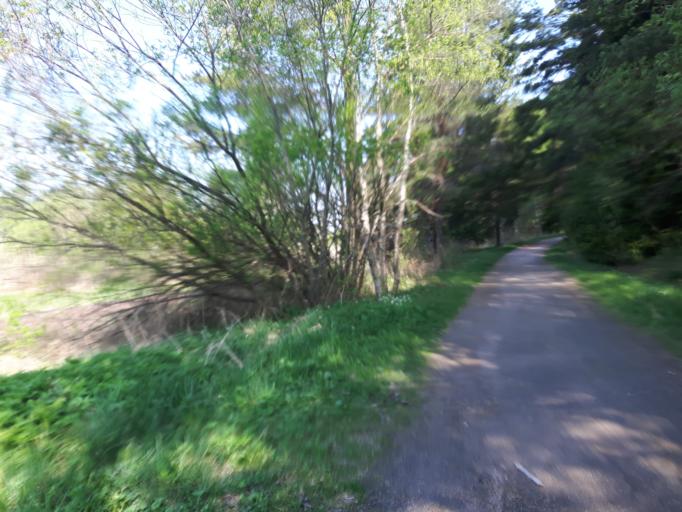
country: FI
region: Uusimaa
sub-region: Helsinki
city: Vantaa
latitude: 60.2298
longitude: 25.1561
